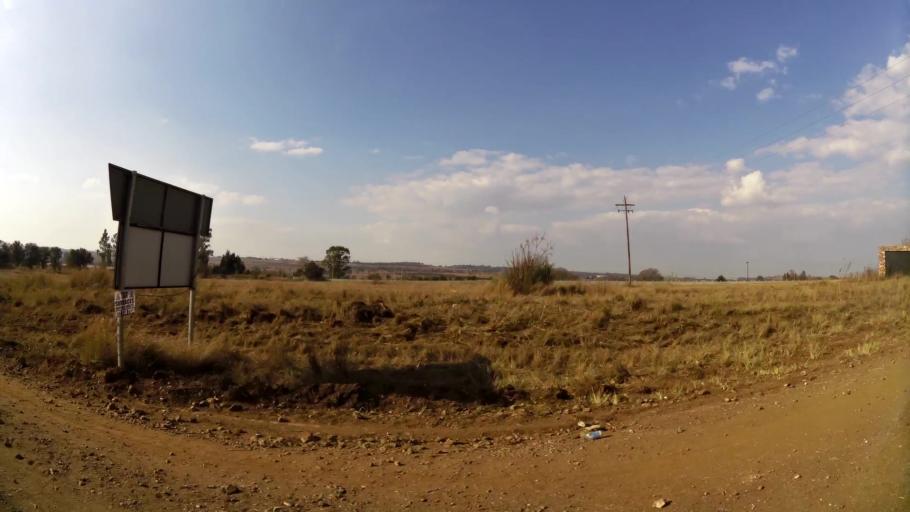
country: ZA
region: Gauteng
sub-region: Ekurhuleni Metropolitan Municipality
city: Tembisa
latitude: -25.9271
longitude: 28.2301
